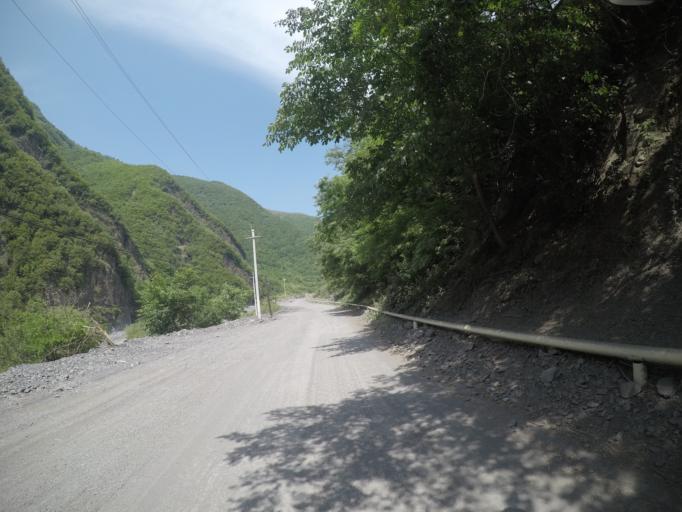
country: AZ
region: Qakh Rayon
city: Qaxbas
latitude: 41.4624
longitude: 47.0314
